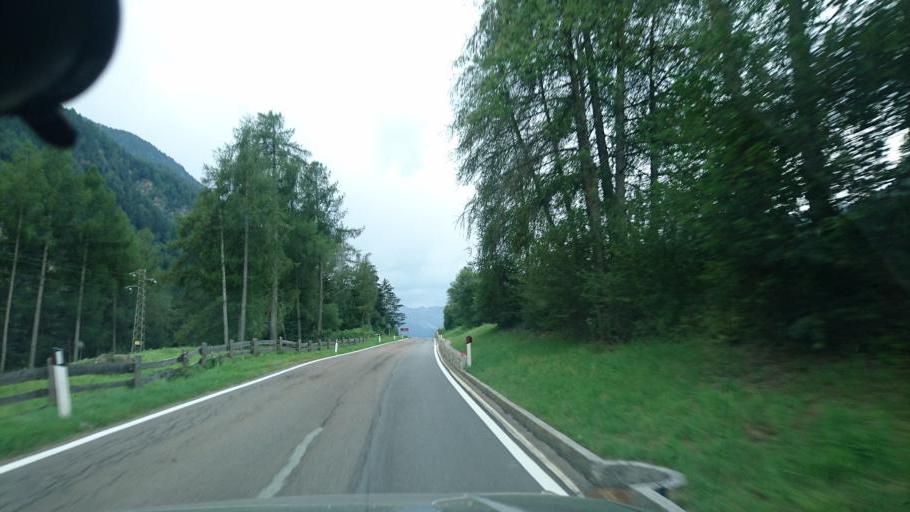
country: IT
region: Trentino-Alto Adige
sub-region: Bolzano
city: Tubre
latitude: 46.6584
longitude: 10.4948
